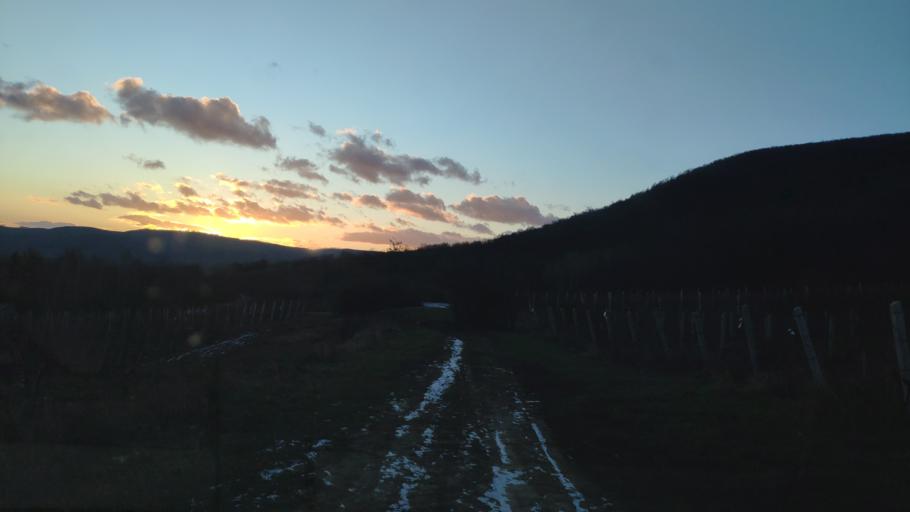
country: HU
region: Borsod-Abauj-Zemplen
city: Olaszliszka
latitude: 48.2770
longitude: 21.3973
